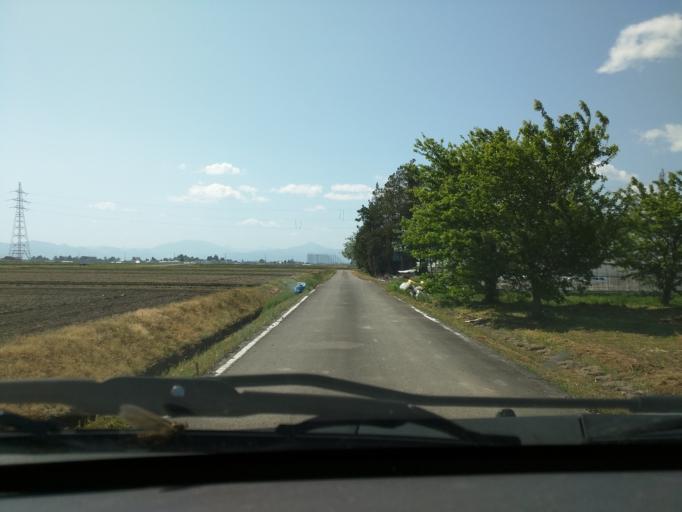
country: JP
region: Fukushima
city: Kitakata
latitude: 37.5785
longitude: 139.8342
